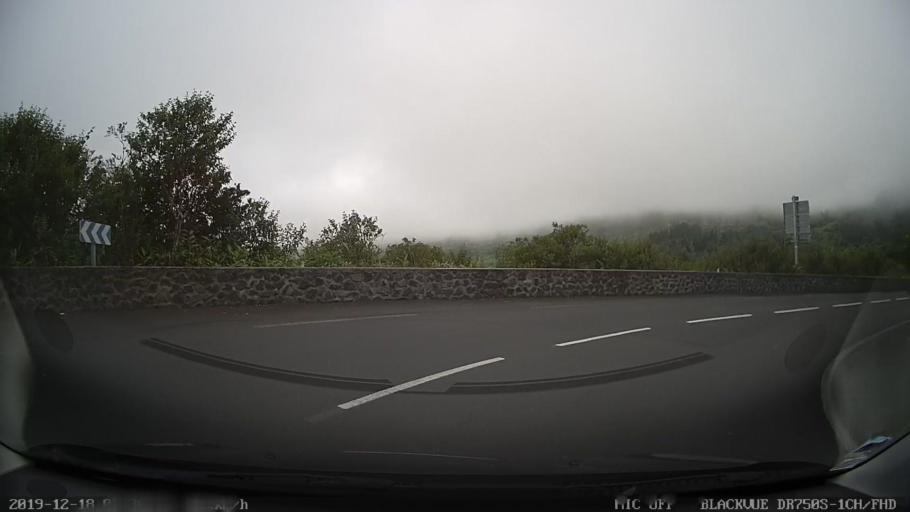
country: RE
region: Reunion
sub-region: Reunion
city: Cilaos
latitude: -21.1543
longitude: 55.6031
